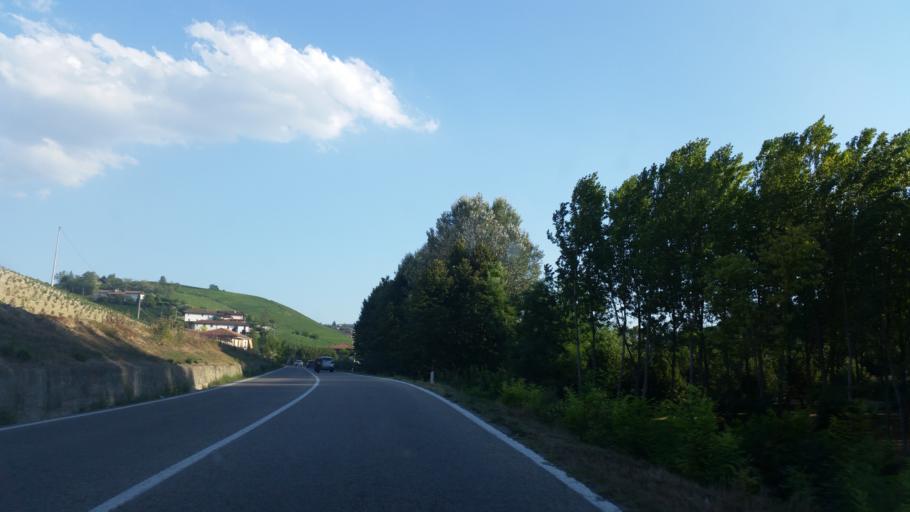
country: IT
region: Piedmont
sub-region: Provincia di Cuneo
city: Barbaresco
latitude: 44.7365
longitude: 8.0940
